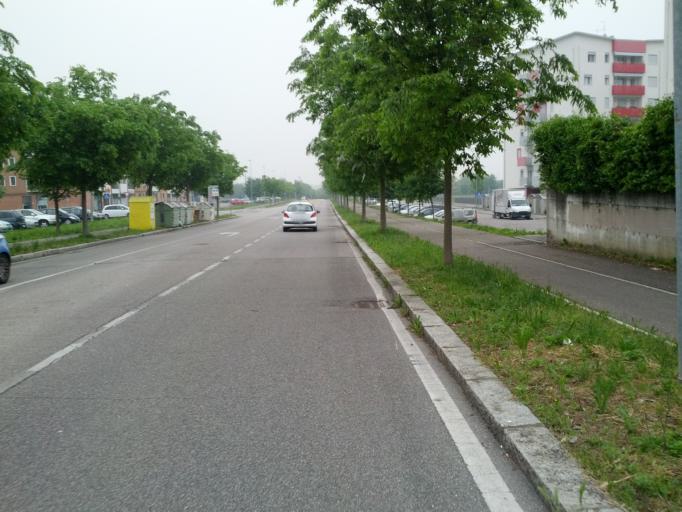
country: IT
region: Veneto
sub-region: Provincia di Verona
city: Montorio
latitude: 45.4353
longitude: 11.0561
